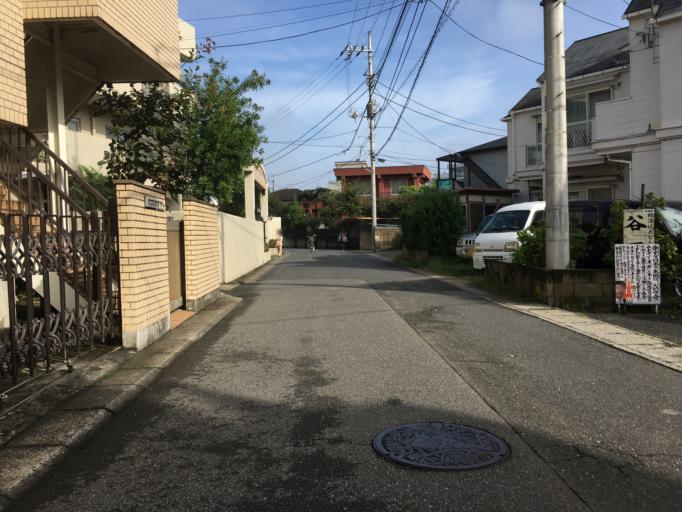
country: JP
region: Chiba
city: Matsudo
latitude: 35.7893
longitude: 139.9002
